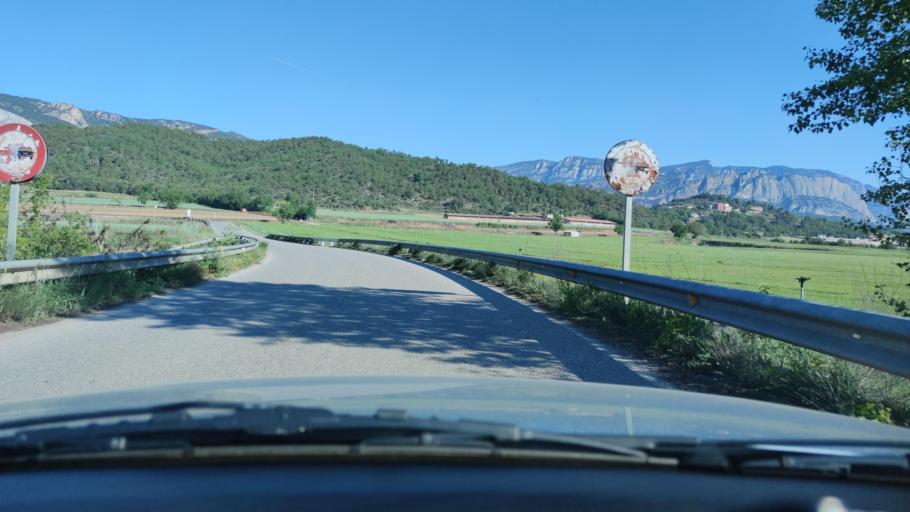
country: ES
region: Catalonia
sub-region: Provincia de Lleida
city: Oliana
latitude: 42.0342
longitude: 1.2900
